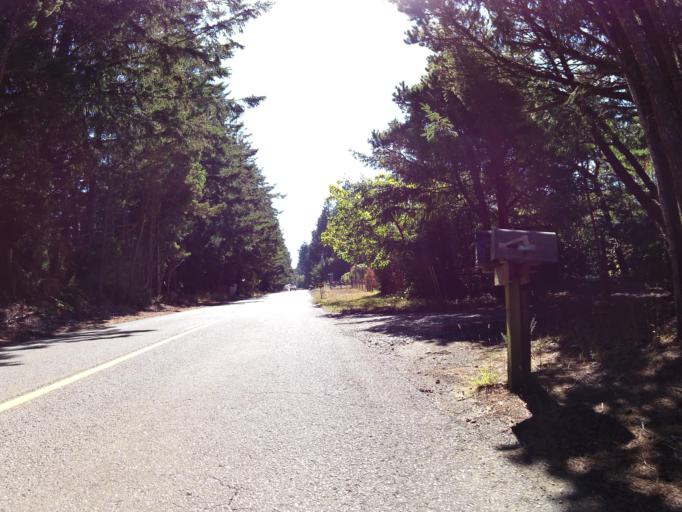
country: US
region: Oregon
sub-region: Coos County
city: Bandon
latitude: 43.1813
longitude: -124.3697
